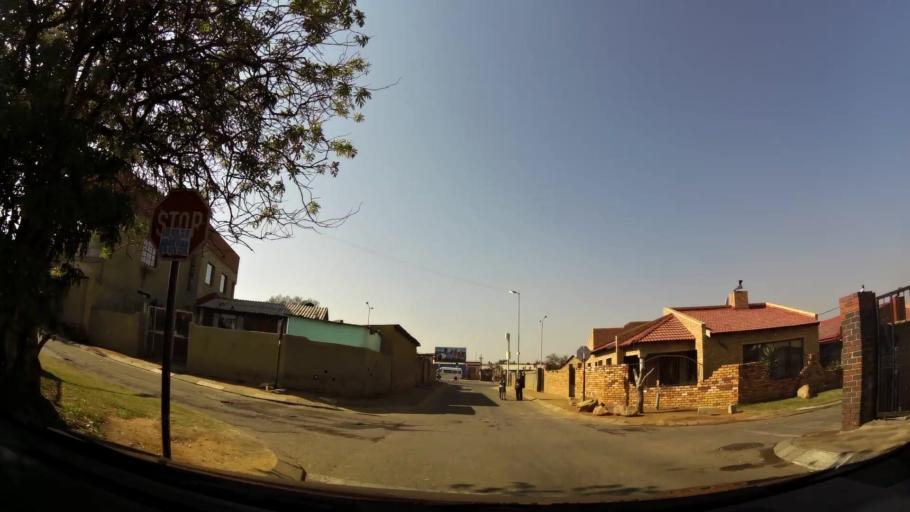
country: ZA
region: Gauteng
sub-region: City of Johannesburg Metropolitan Municipality
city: Soweto
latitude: -26.2461
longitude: 27.9481
